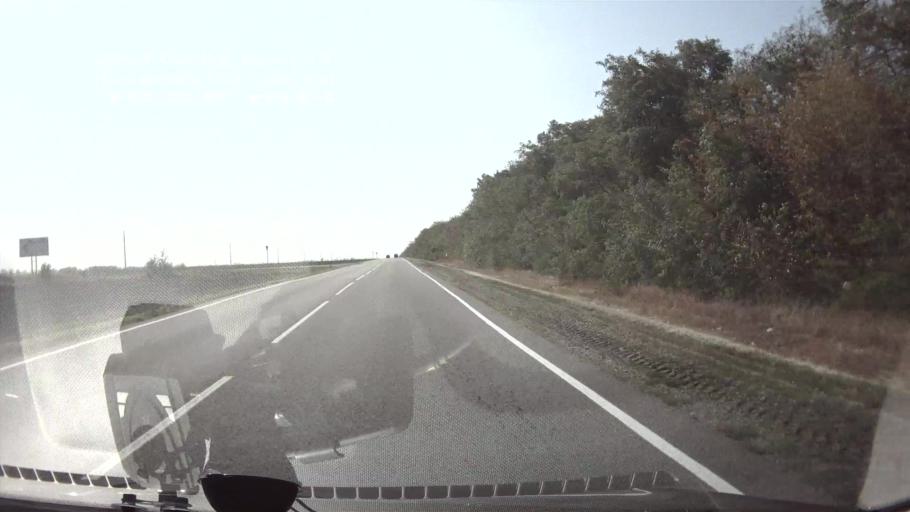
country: RU
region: Krasnodarskiy
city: Novopokrovskaya
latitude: 45.8771
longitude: 40.7208
